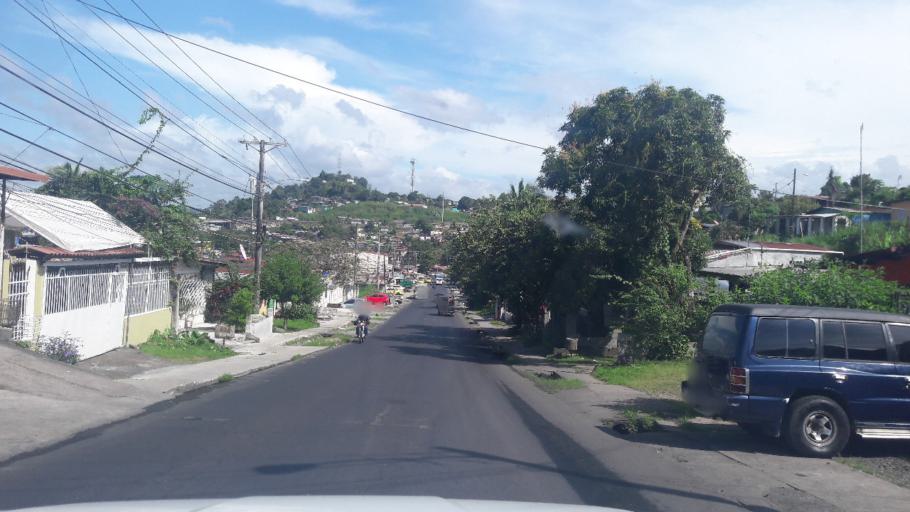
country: PA
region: Panama
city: San Miguelito
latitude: 9.0660
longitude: -79.4882
